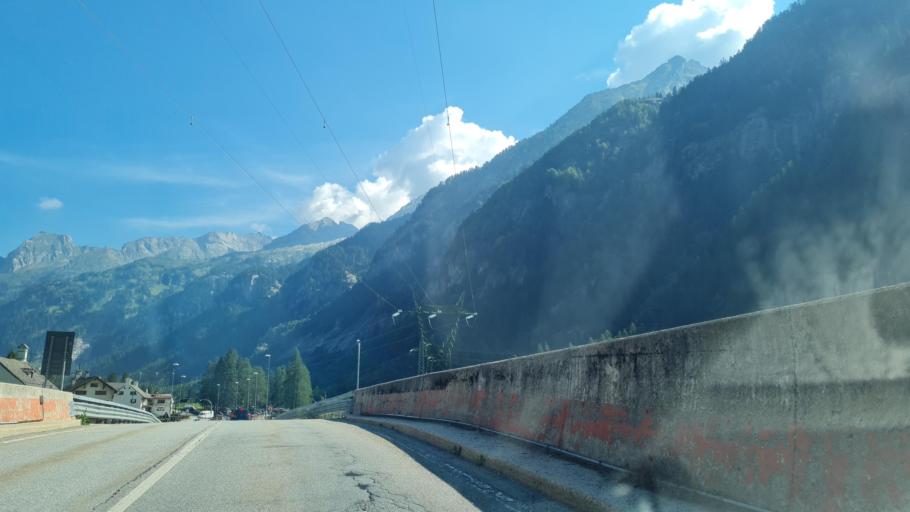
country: IT
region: Piedmont
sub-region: Provincia Verbano-Cusio-Ossola
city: Formazza
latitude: 46.3422
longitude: 8.4246
